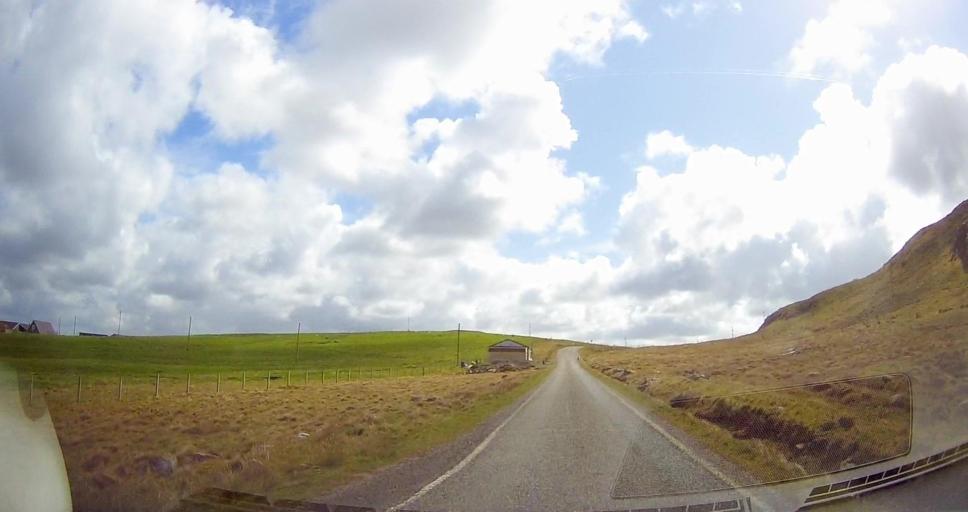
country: GB
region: Scotland
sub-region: Shetland Islands
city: Lerwick
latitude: 60.5459
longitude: -1.3410
